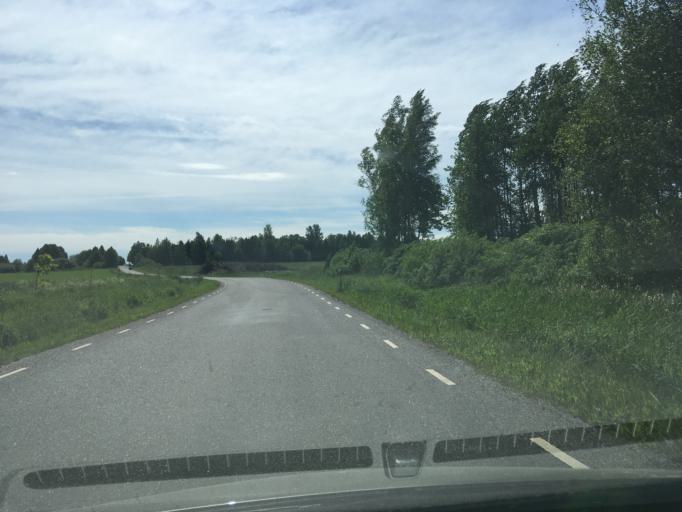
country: EE
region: Paernumaa
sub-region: Audru vald
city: Audru
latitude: 58.4439
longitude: 24.3911
